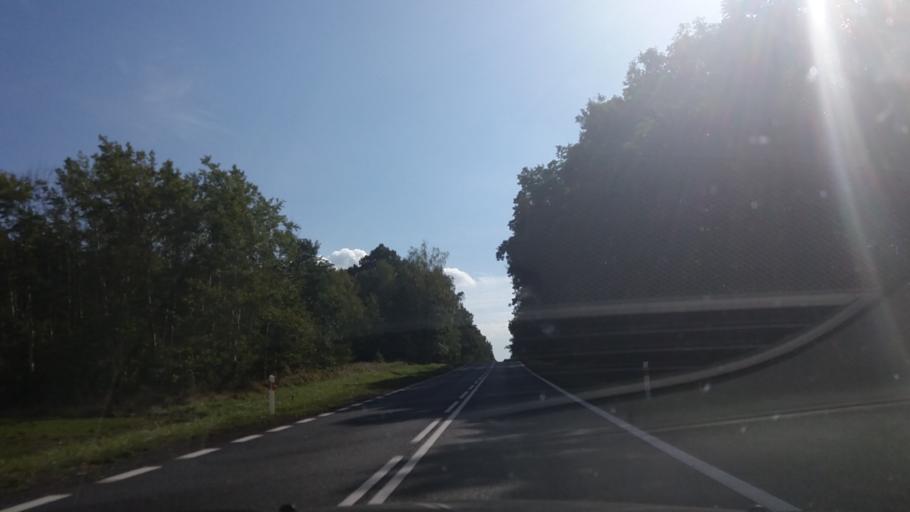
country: PL
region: Lower Silesian Voivodeship
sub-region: Powiat lubinski
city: Osiek
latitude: 51.3441
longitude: 16.2853
